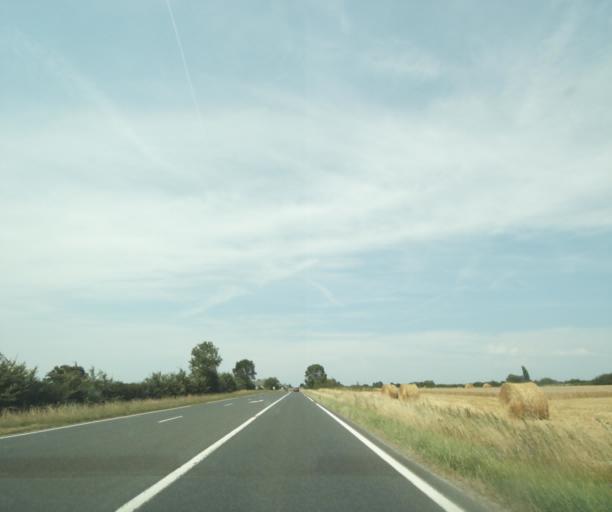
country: FR
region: Centre
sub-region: Departement d'Indre-et-Loire
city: Sorigny
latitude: 47.1871
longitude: 0.6631
